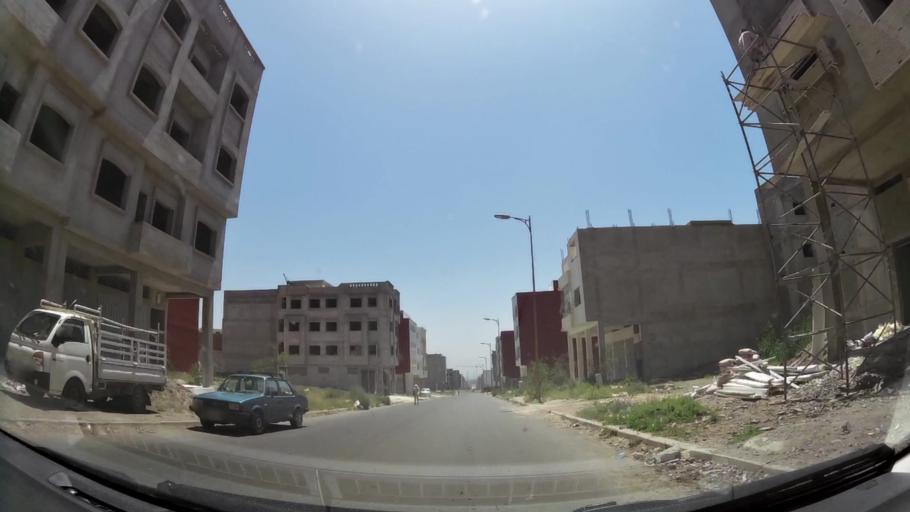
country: MA
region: Oued ed Dahab-Lagouira
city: Dakhla
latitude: 30.4415
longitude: -9.5565
